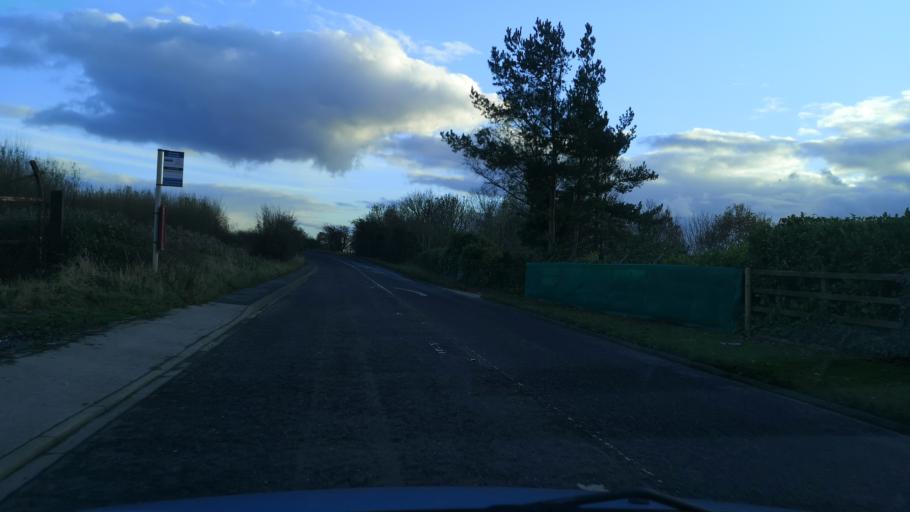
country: GB
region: England
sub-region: City and Borough of Wakefield
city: Ossett
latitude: 53.7123
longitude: -1.5706
